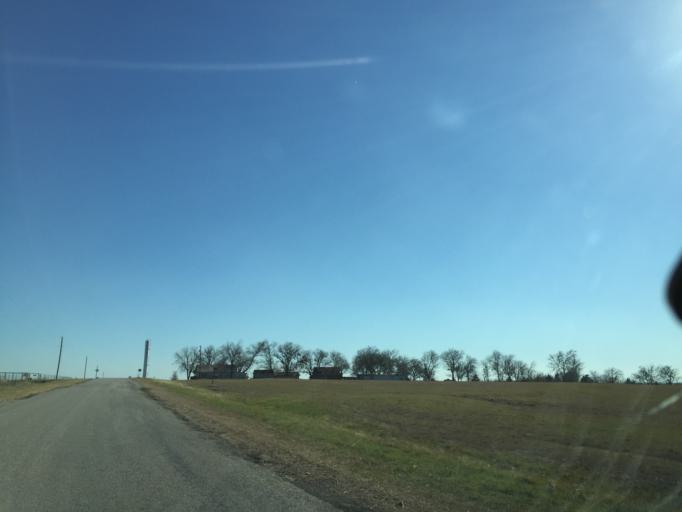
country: US
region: Texas
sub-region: Williamson County
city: Taylor
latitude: 30.5738
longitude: -97.3112
